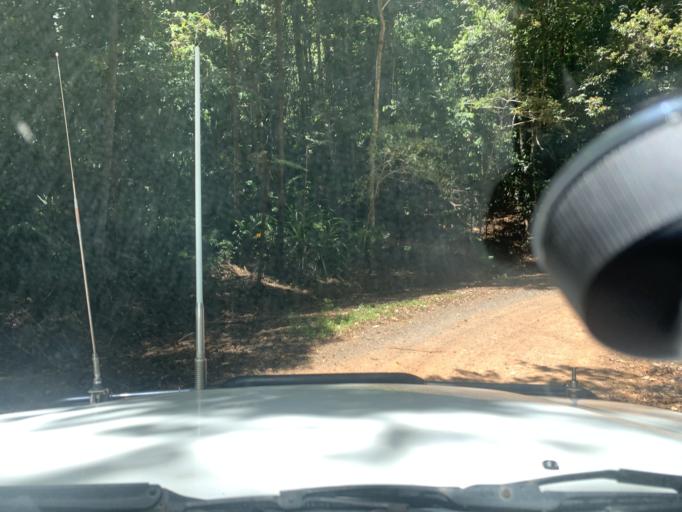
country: AU
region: Queensland
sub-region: Cairns
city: Woree
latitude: -16.9743
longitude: 145.6509
